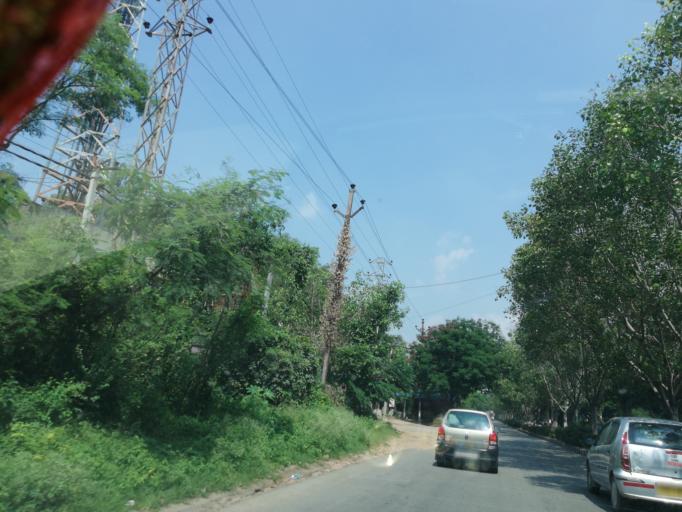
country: IN
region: Telangana
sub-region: Medak
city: Serilingampalle
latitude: 17.4652
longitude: 78.3337
